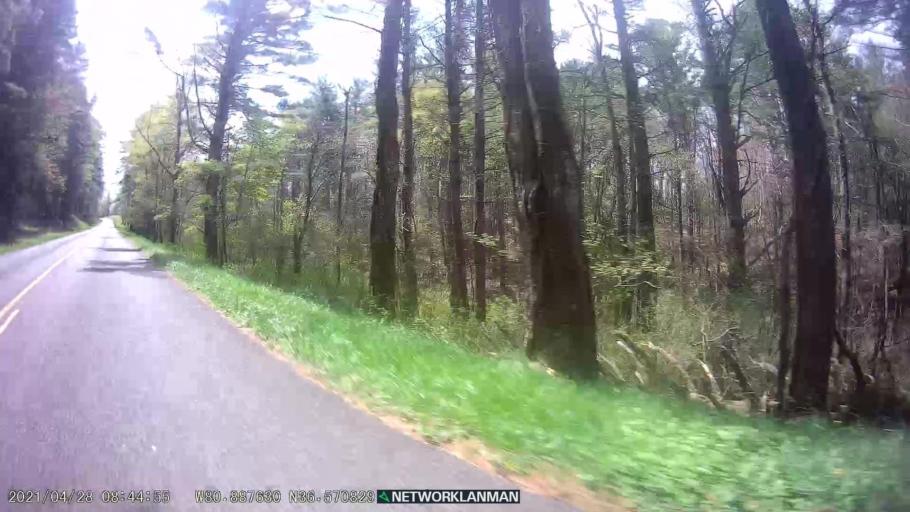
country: US
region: Virginia
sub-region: City of Galax
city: Galax
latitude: 36.5706
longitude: -80.8873
